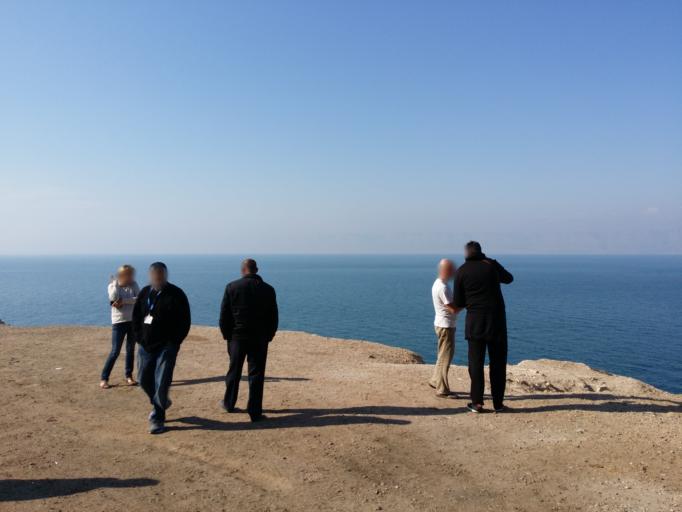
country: JO
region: Karak
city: Al Qasr
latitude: 31.4312
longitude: 35.5627
